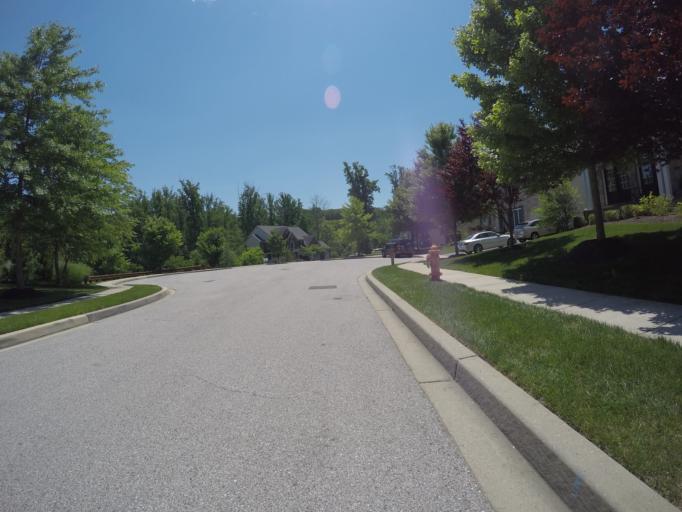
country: US
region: Maryland
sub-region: Howard County
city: Ilchester
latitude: 39.2394
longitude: -76.7822
